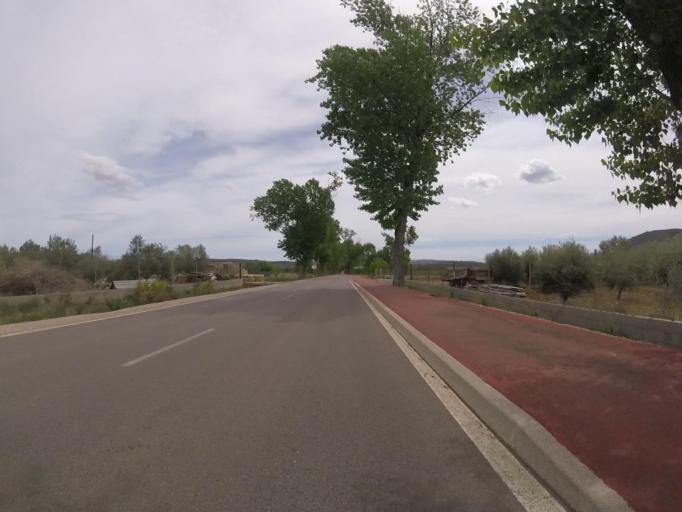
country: ES
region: Valencia
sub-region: Provincia de Castello
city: Cabanes
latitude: 40.1639
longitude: 0.0196
